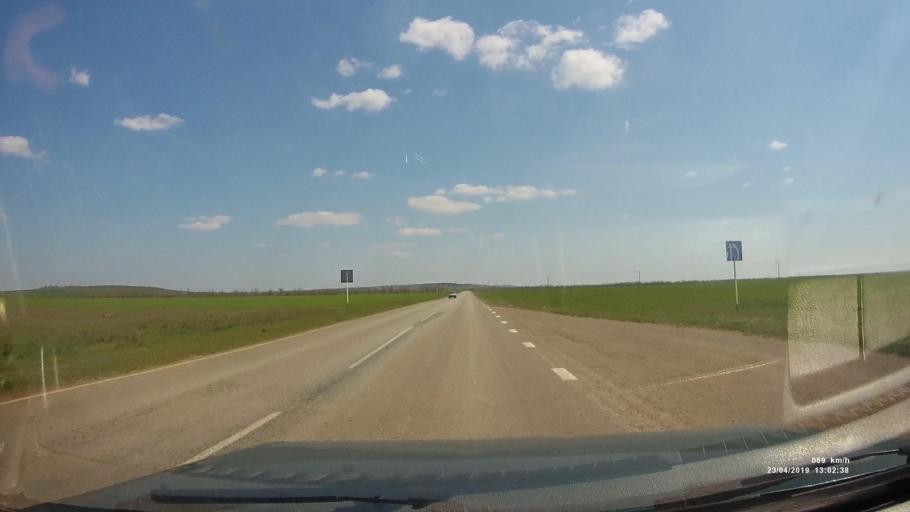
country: RU
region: Kalmykiya
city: Yashalta
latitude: 46.5998
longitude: 42.6720
